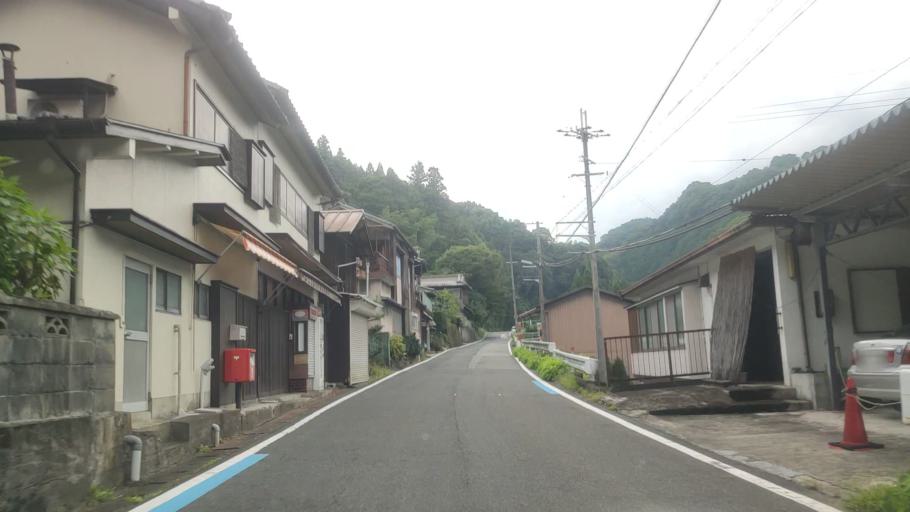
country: JP
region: Wakayama
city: Hashimoto
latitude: 34.2676
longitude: 135.5535
